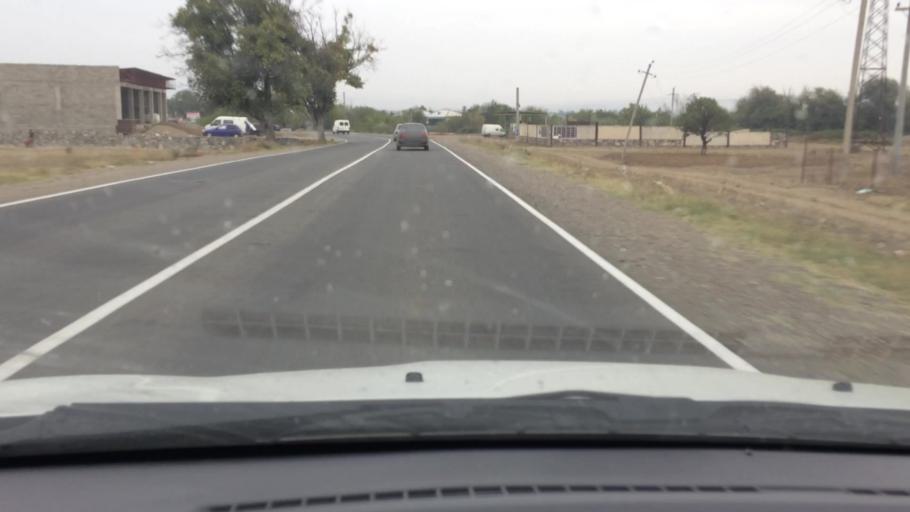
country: GE
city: Naghvarevi
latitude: 41.3932
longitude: 44.8276
